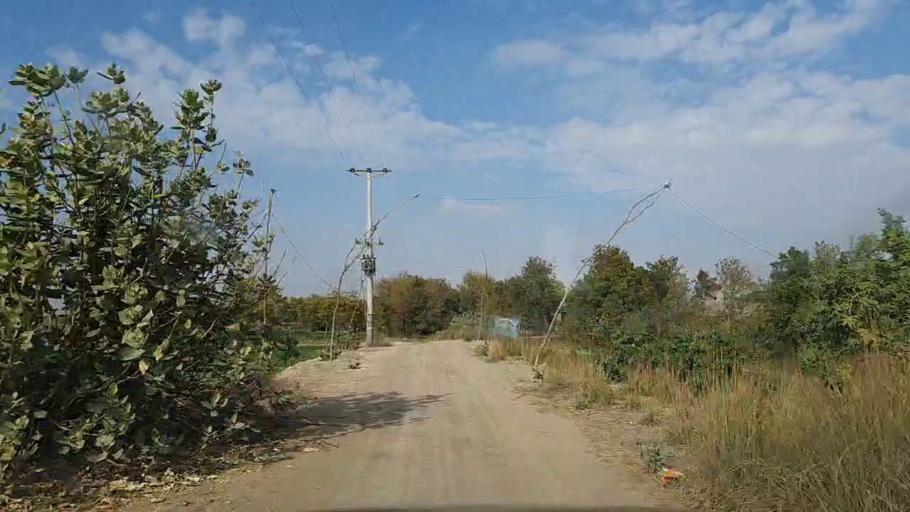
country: PK
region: Sindh
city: Sanghar
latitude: 26.2777
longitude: 69.0092
